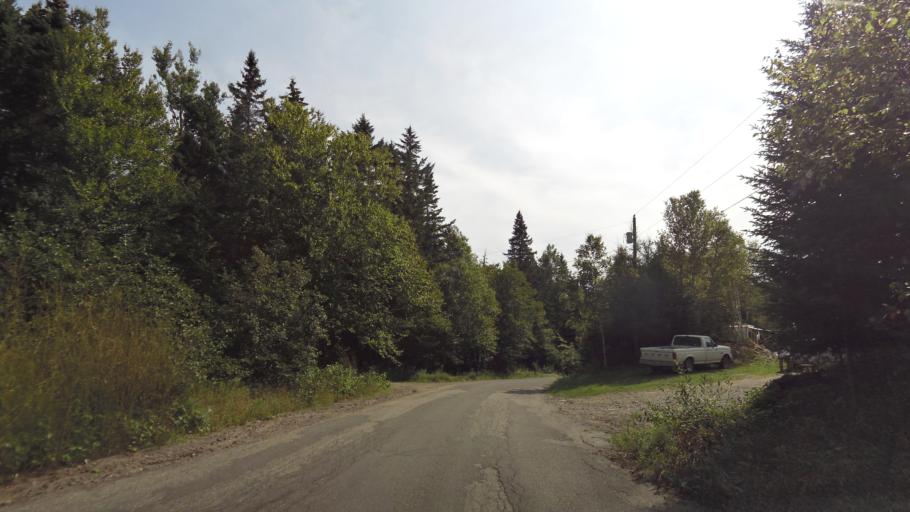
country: CA
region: New Brunswick
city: Hampton
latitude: 45.5586
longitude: -65.8427
